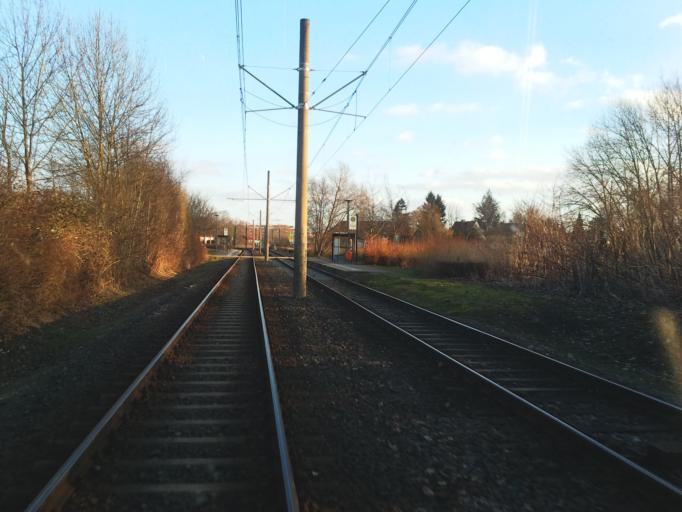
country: DE
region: Mecklenburg-Vorpommern
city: Dierkow-West
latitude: 54.1096
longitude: 12.1543
